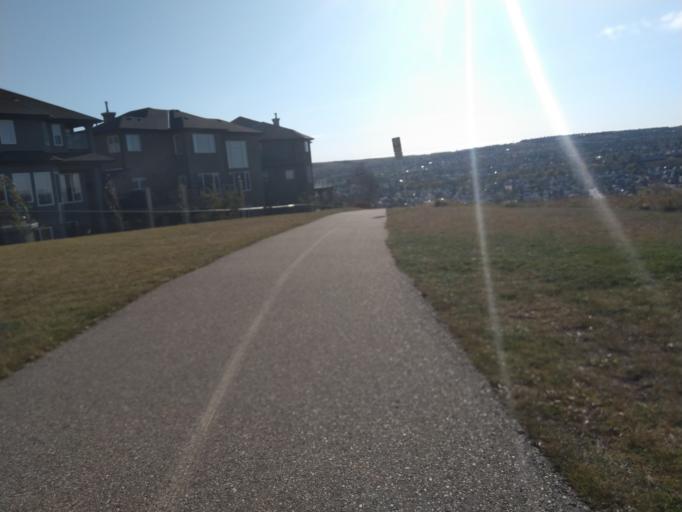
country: CA
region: Alberta
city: Calgary
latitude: 51.1527
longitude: -114.0933
